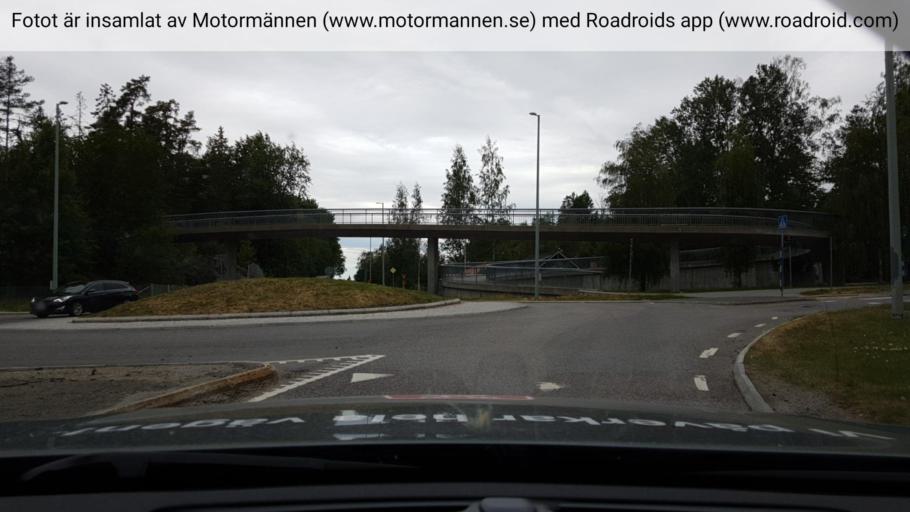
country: SE
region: Stockholm
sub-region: Huddinge Kommun
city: Huddinge
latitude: 59.2209
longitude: 18.0081
